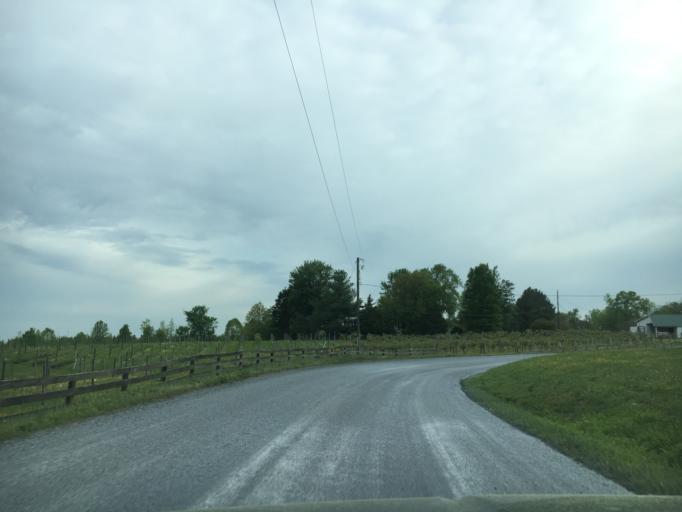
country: US
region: Virginia
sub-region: Campbell County
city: Brookneal
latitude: 36.9313
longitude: -78.9494
